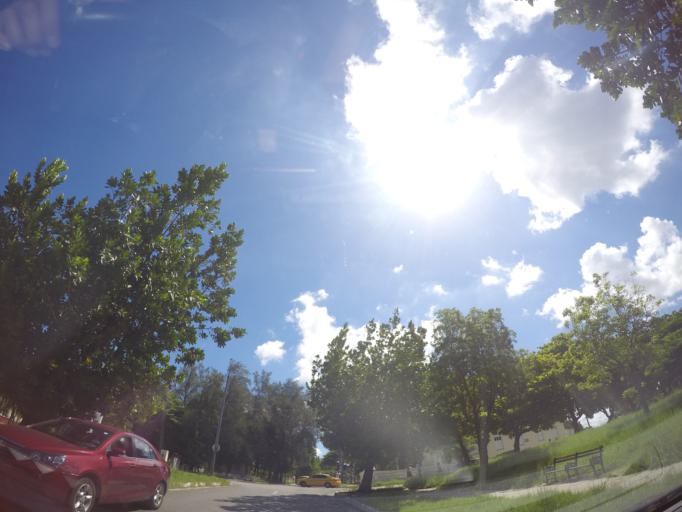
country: CU
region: La Habana
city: La Habana Vieja
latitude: 23.1446
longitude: -82.3436
